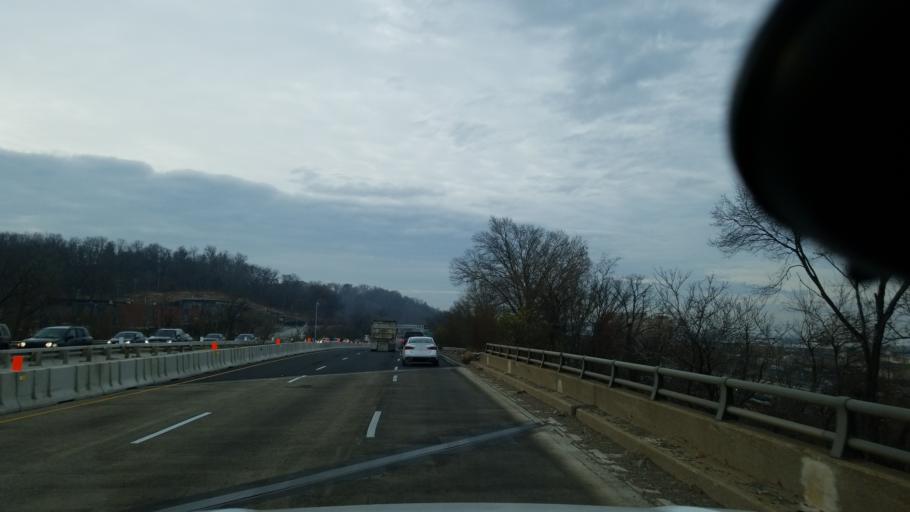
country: US
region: Maryland
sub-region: Prince George's County
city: Glassmanor
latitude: 38.8601
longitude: -77.0032
